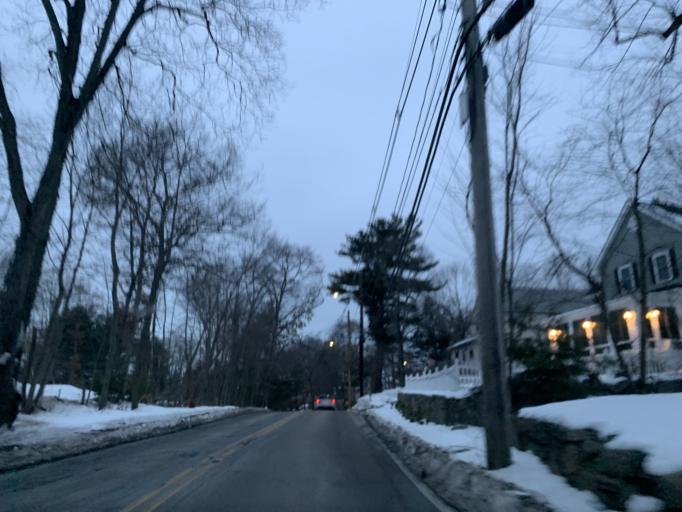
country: US
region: Massachusetts
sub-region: Norfolk County
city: Canton
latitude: 42.1514
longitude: -71.1354
